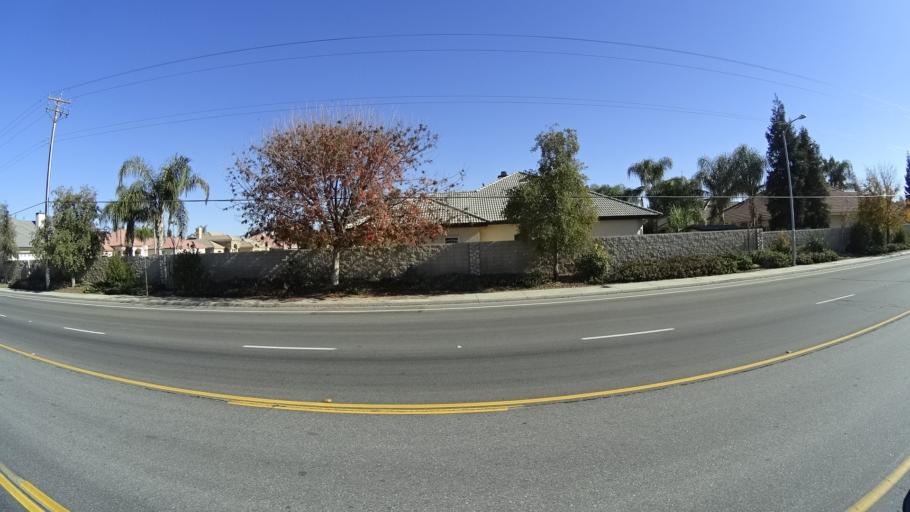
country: US
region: California
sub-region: Kern County
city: Greenfield
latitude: 35.2755
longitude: -119.0566
